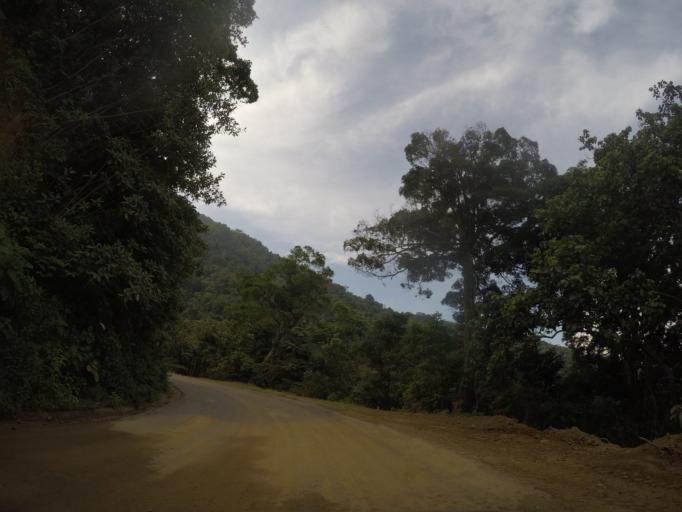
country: MX
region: Oaxaca
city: Pluma Hidalgo
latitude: 15.9484
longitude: -96.4406
